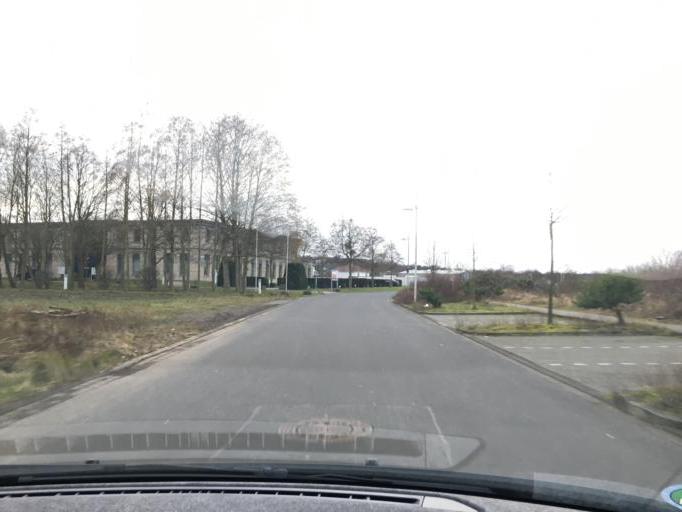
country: DE
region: North Rhine-Westphalia
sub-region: Regierungsbezirk Koln
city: Kerpen
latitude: 50.8937
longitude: 6.6829
